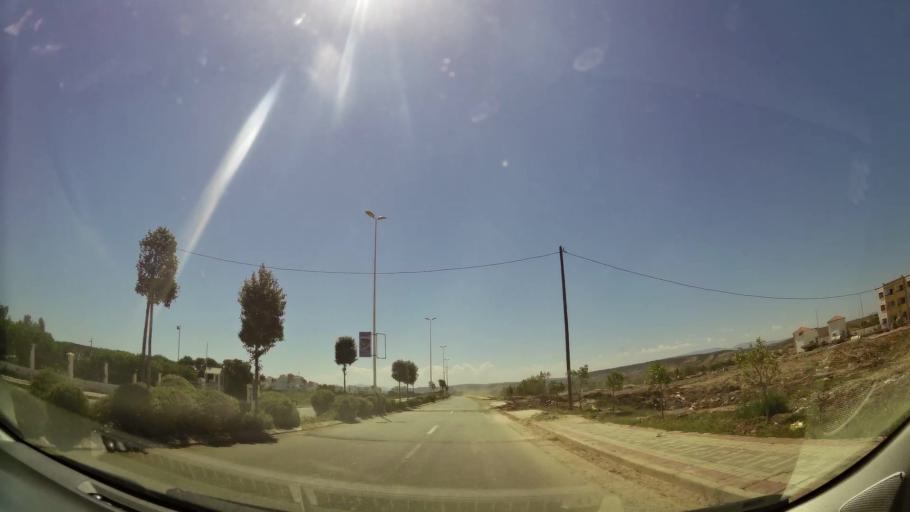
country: MA
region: Oriental
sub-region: Berkane-Taourirt
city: Madagh
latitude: 35.1026
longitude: -2.3124
